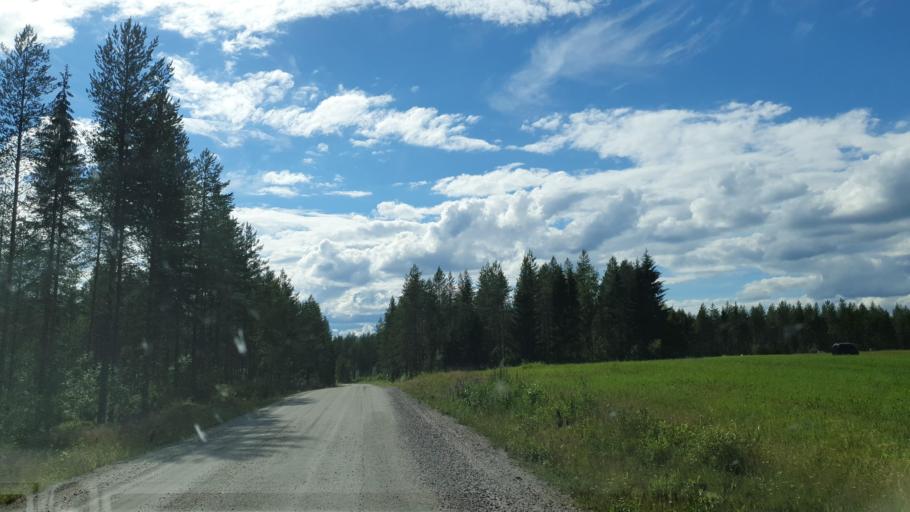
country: FI
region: Kainuu
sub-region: Kehys-Kainuu
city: Kuhmo
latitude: 64.1371
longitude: 29.6758
